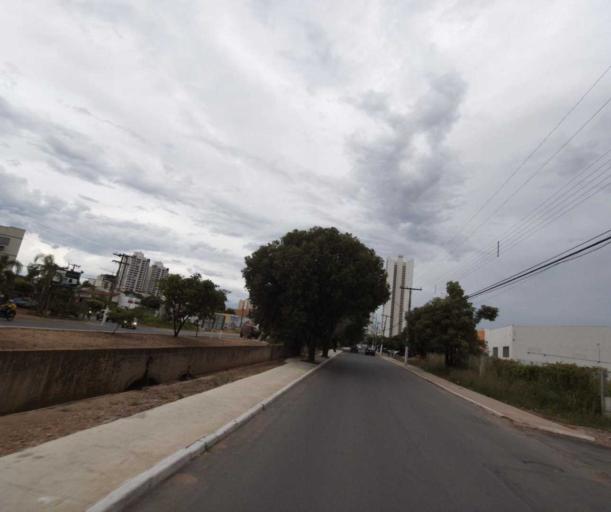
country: BR
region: Mato Grosso
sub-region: Cuiaba
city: Cuiaba
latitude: -15.6184
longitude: -56.0767
